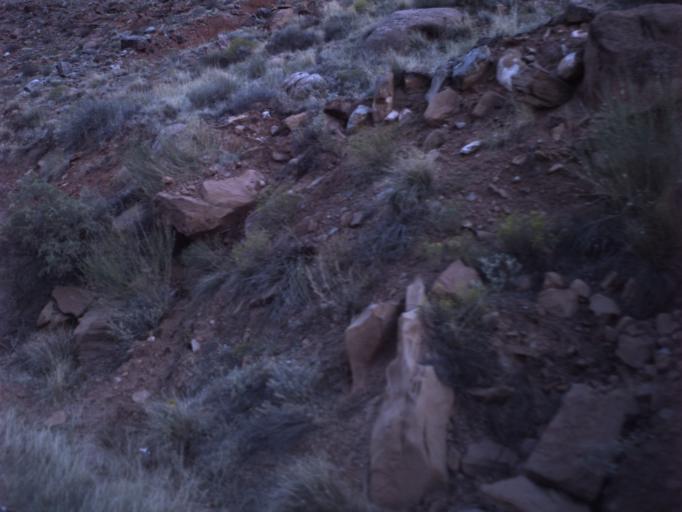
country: US
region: Utah
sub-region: Grand County
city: Moab
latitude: 38.6319
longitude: -109.4891
